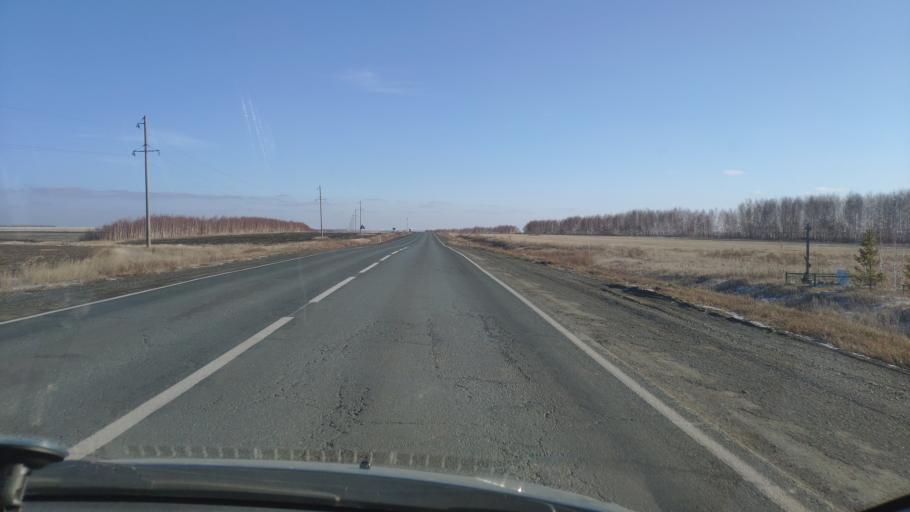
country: RU
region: Orenburg
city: Novorudnyy
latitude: 51.4319
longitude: 57.9127
